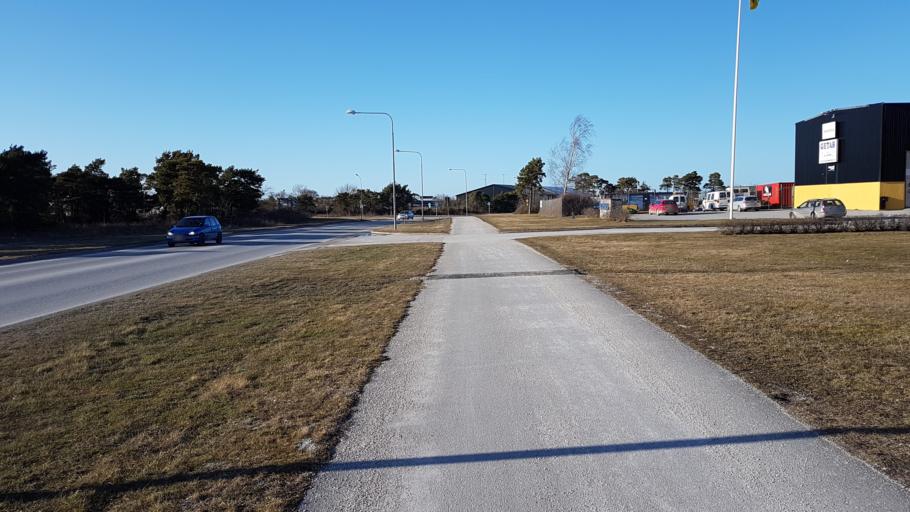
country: SE
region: Gotland
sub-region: Gotland
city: Visby
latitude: 57.6398
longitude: 18.3275
